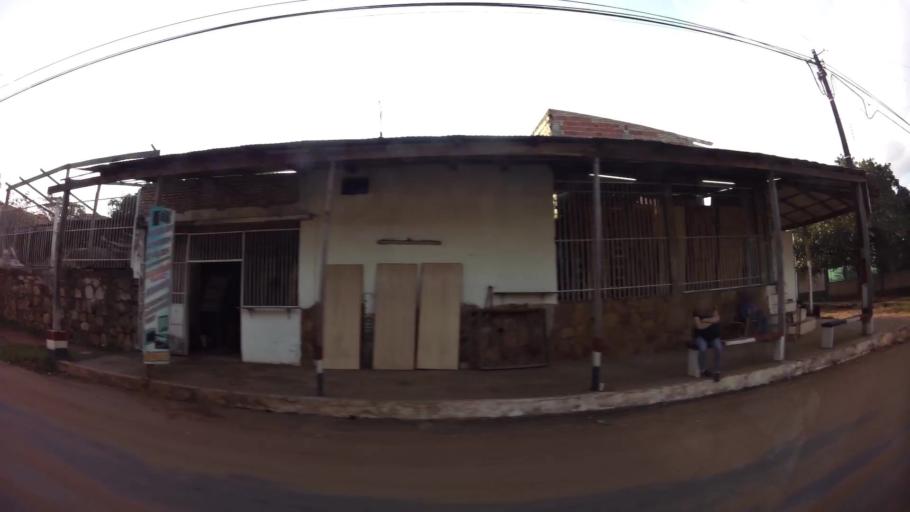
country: PY
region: Central
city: Fernando de la Mora
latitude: -25.3528
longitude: -57.5280
